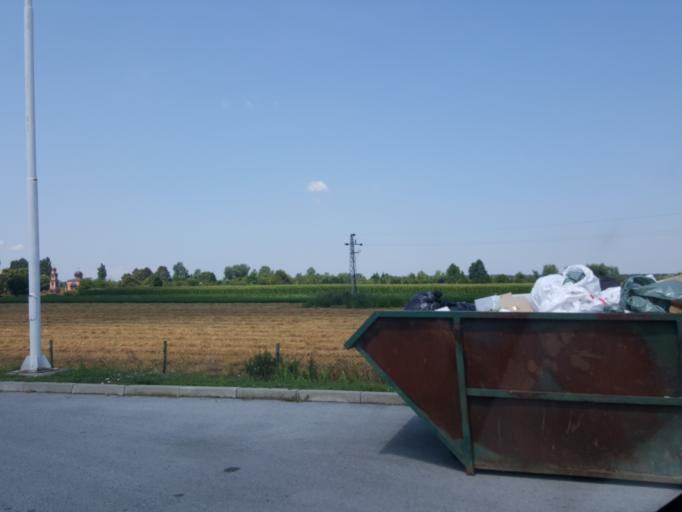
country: RS
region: Autonomna Pokrajina Vojvodina
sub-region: Sremski Okrug
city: Sid
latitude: 45.0495
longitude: 19.1876
